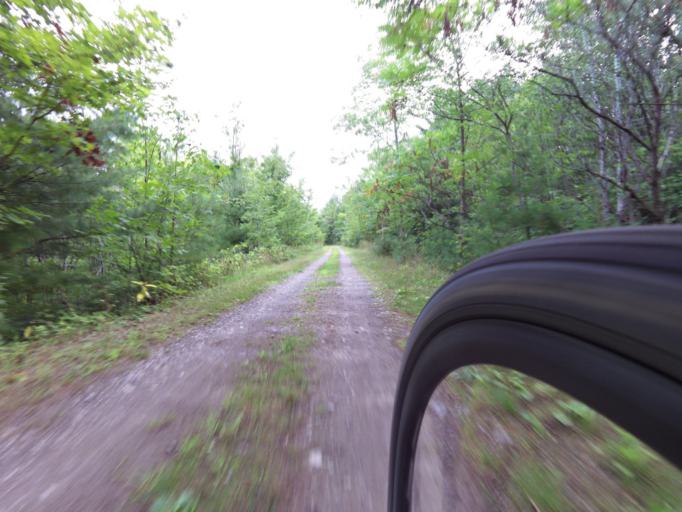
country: CA
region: Ontario
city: Gananoque
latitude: 44.5863
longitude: -76.3109
